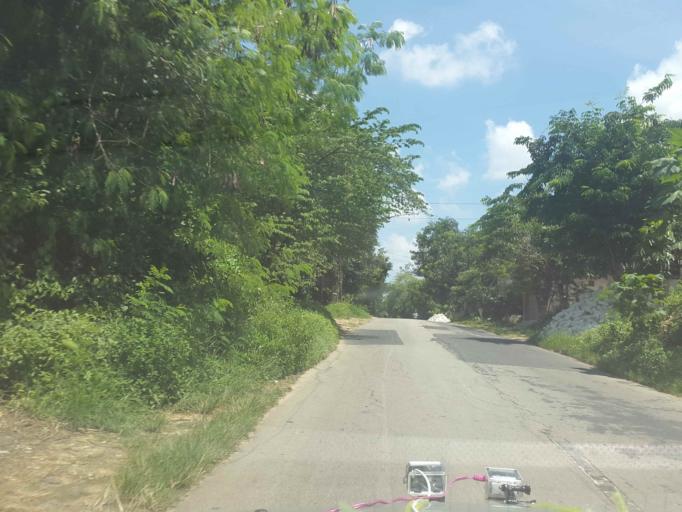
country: ID
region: East Java
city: Ganjur
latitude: -6.9766
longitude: 113.8614
